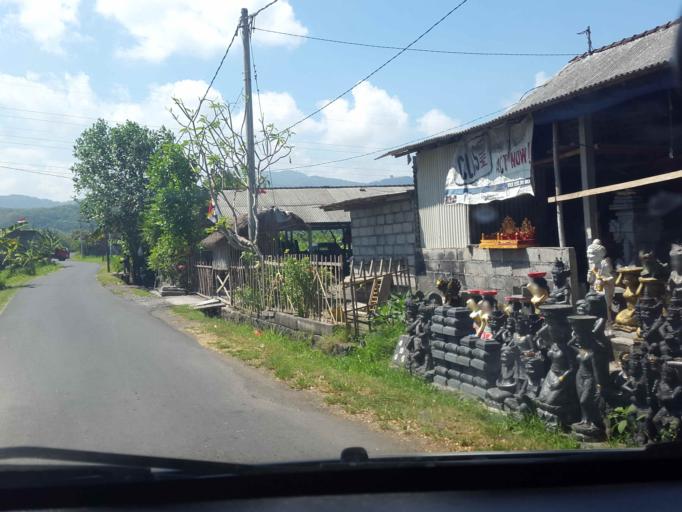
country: ID
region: Bali
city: Dawan
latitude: -8.5555
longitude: 115.4482
